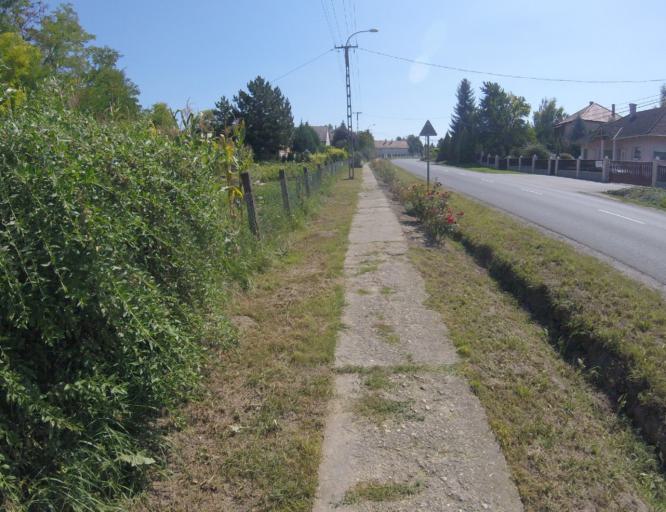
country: HU
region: Fejer
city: Pazmand
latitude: 47.2829
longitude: 18.6546
